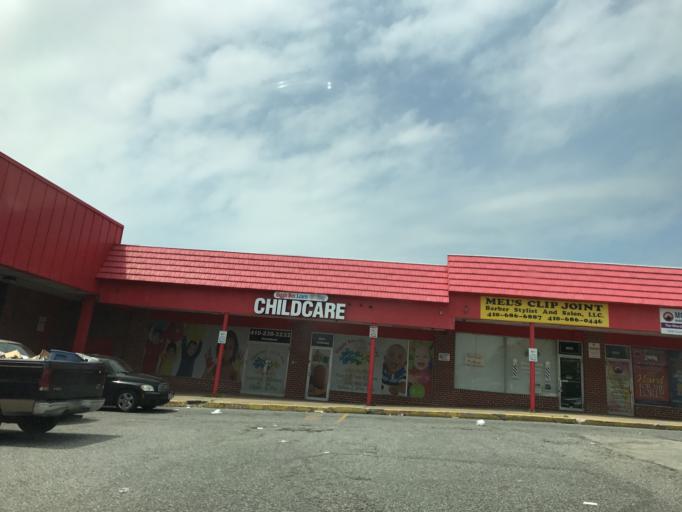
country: US
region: Maryland
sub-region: Baltimore County
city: Middle River
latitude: 39.3090
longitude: -76.4482
